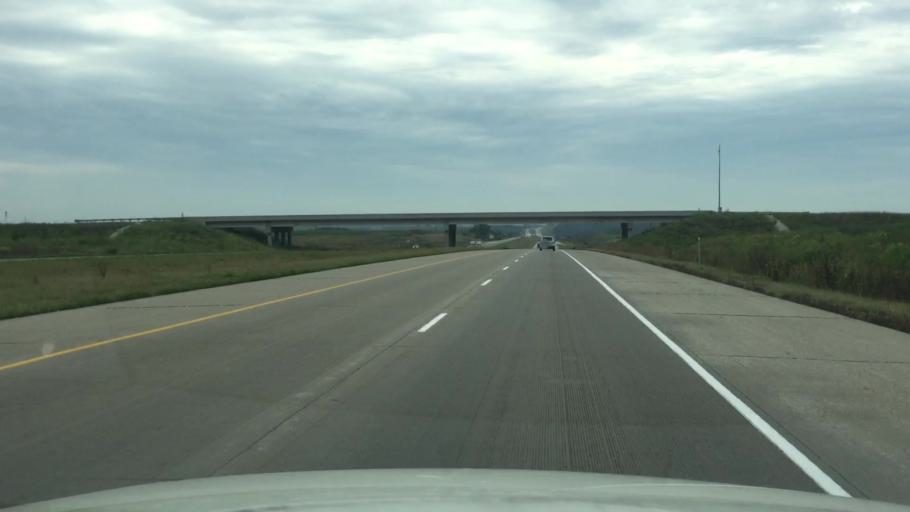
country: US
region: Iowa
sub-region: Warren County
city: Norwalk
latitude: 41.4844
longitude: -93.7805
